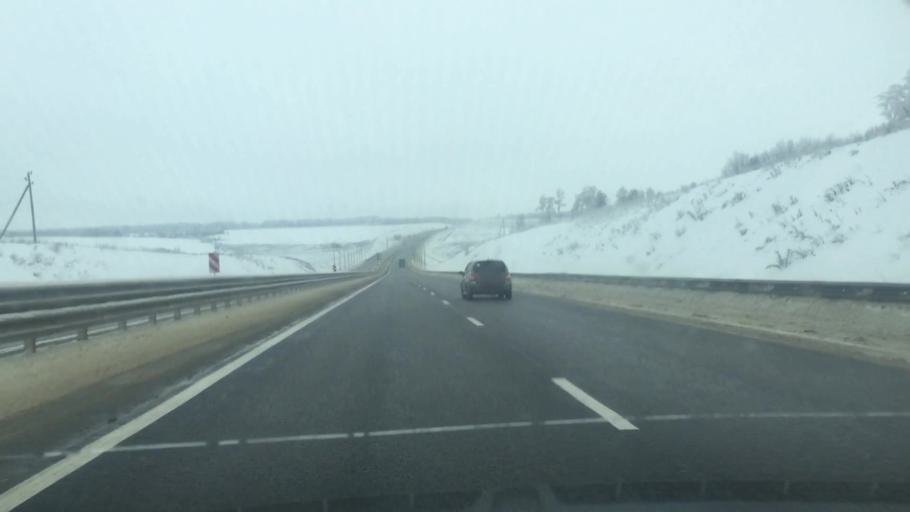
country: RU
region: Lipetsk
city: Stanovoye
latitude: 52.8698
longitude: 38.2817
